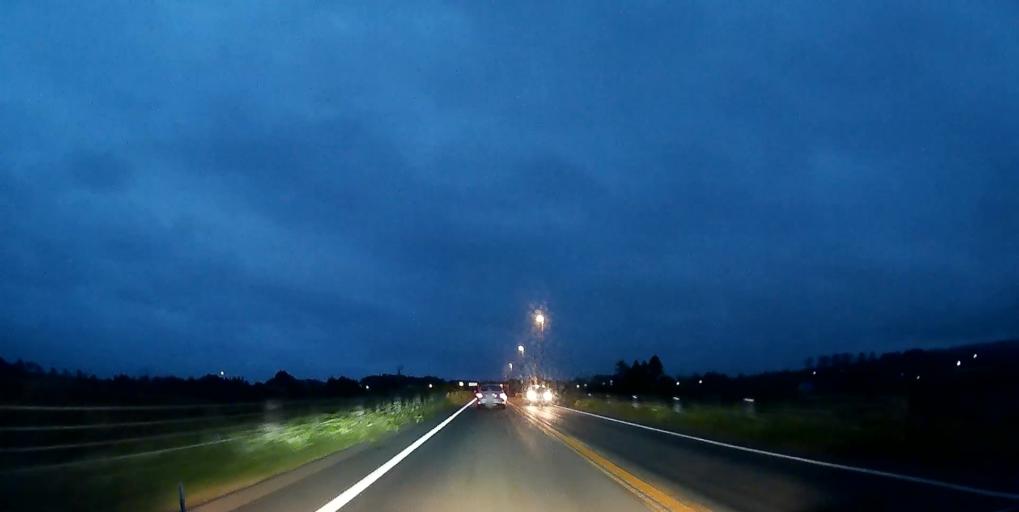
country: JP
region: Hokkaido
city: Nanae
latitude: 42.2108
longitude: 140.3938
